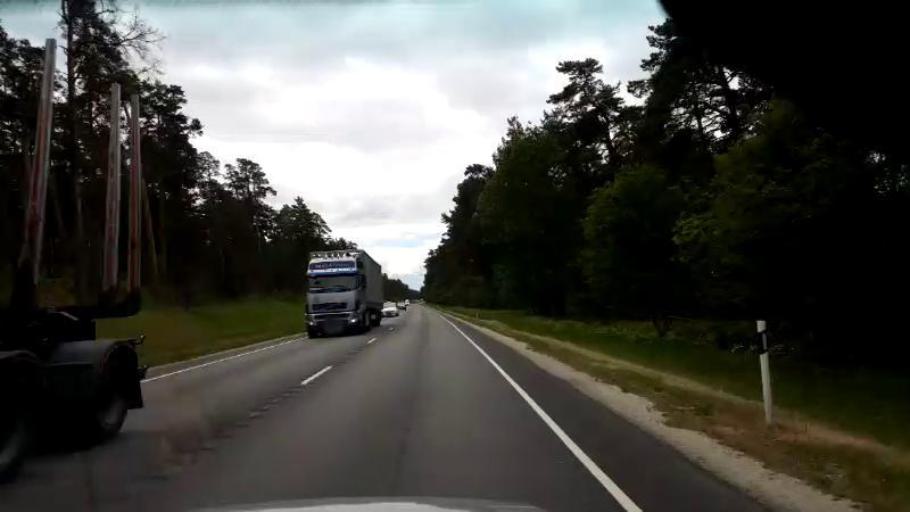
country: EE
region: Paernumaa
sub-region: Paernu linn
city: Parnu
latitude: 58.1714
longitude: 24.4951
